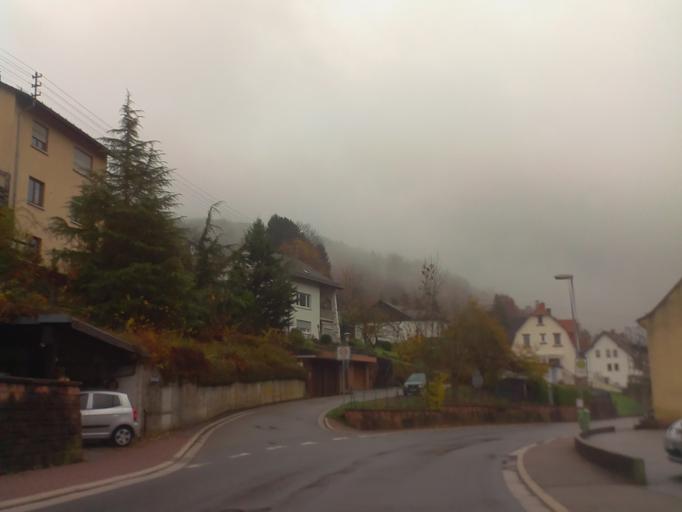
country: DE
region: Baden-Wuerttemberg
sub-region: Karlsruhe Region
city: Heiligkreuzsteinach
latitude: 49.4658
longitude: 8.8040
